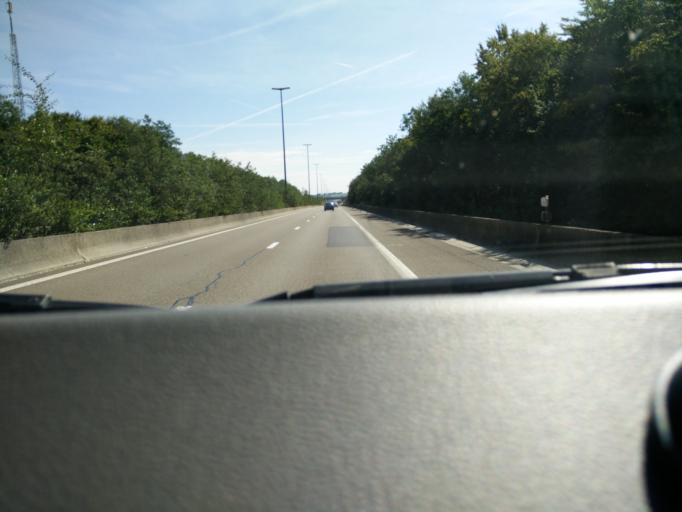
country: BE
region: Wallonia
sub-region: Province du Luxembourg
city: Neufchateau
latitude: 49.8823
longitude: 5.4335
